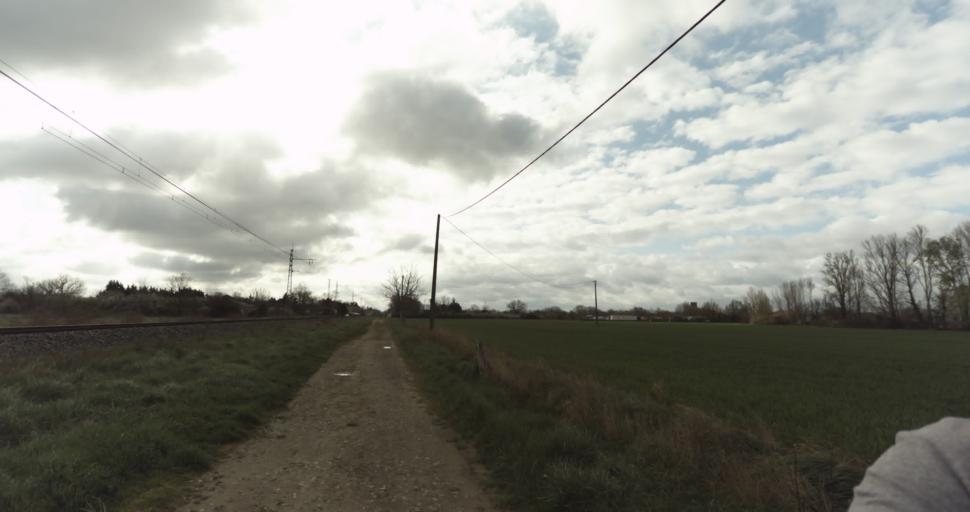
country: FR
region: Midi-Pyrenees
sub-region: Departement de la Haute-Garonne
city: Miremont
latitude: 43.3751
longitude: 1.4422
